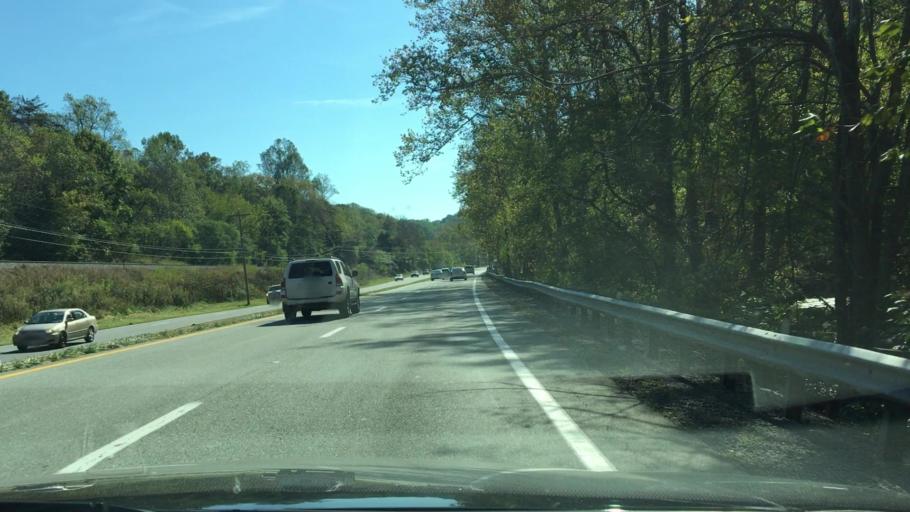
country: US
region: Virginia
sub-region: Roanoke County
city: Narrows
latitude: 37.1287
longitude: -79.9635
